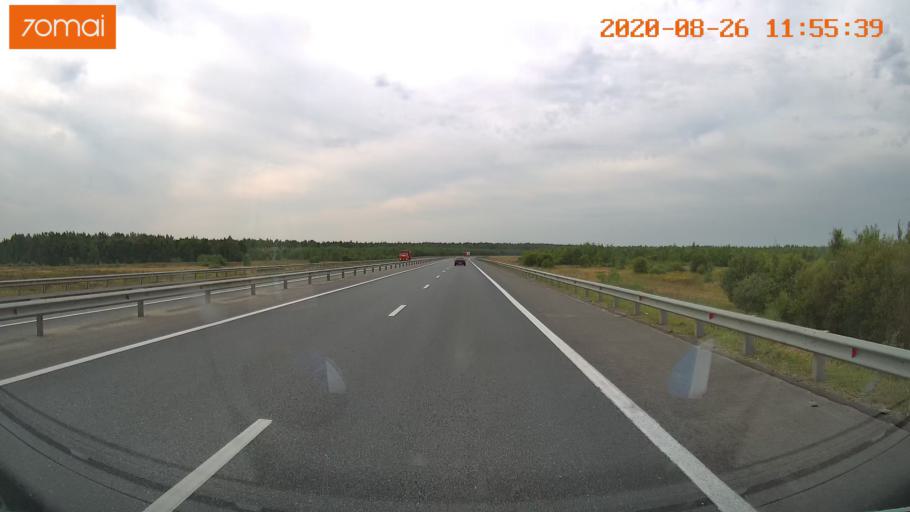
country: RU
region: Rjazan
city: Kiritsy
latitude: 54.2702
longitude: 40.3928
